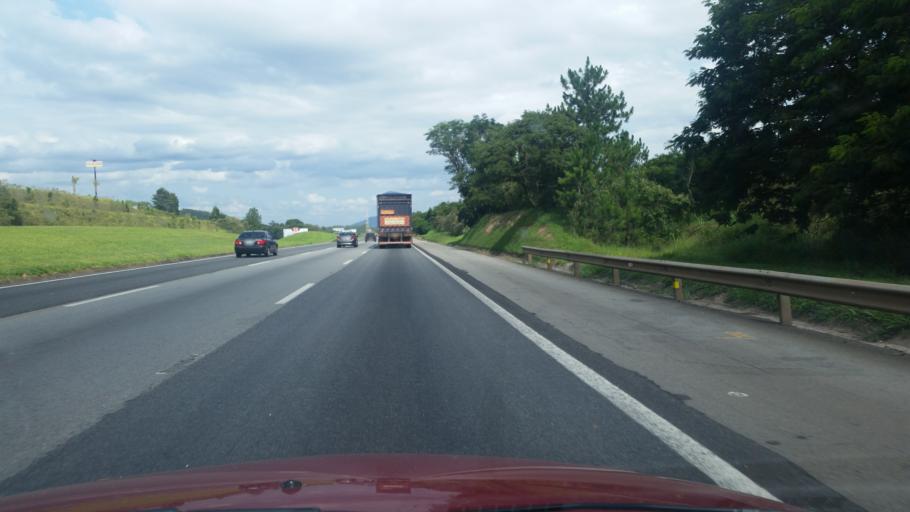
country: BR
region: Sao Paulo
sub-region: Sao Roque
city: Sao Roque
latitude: -23.4199
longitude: -47.1998
